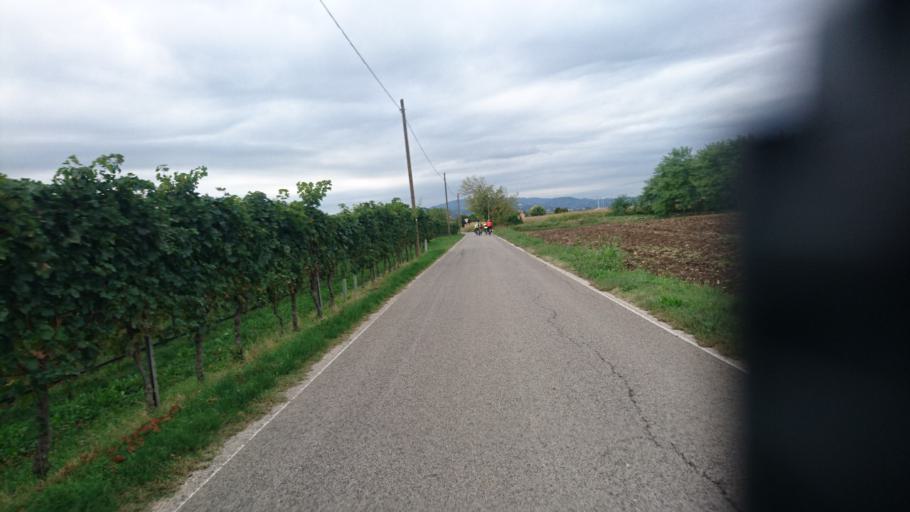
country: IT
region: Veneto
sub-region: Provincia di Vicenza
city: Montorso Vicentino
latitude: 45.4932
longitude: 11.3762
